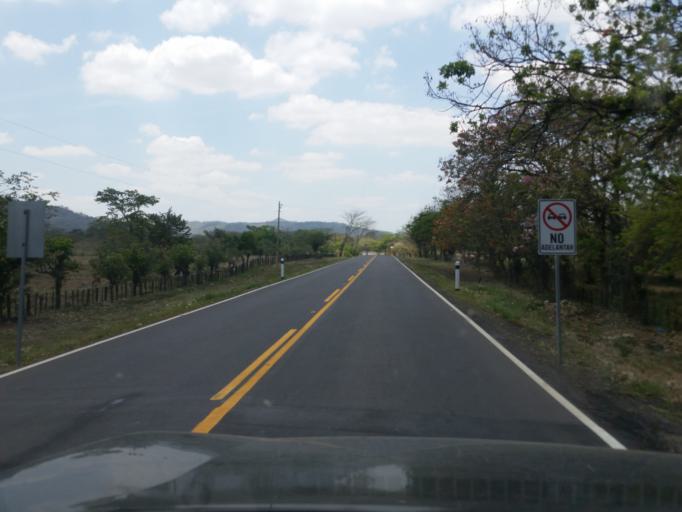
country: NI
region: Boaco
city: Boaco
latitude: 12.5052
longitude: -85.5869
